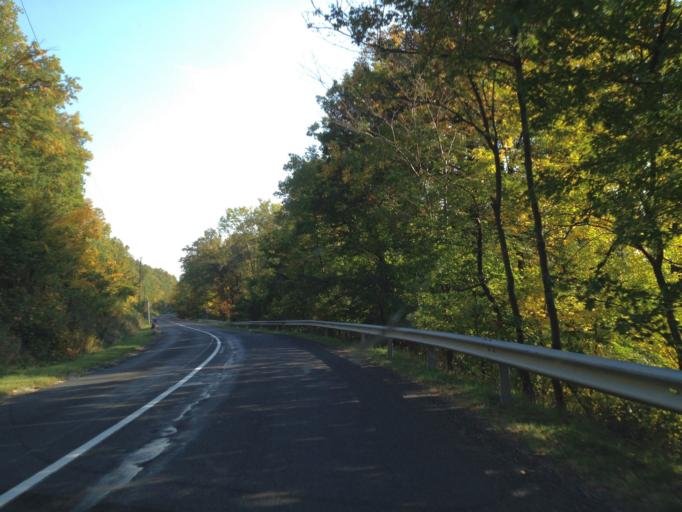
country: HU
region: Pest
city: Pilisszentkereszt
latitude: 47.7116
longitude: 18.8787
